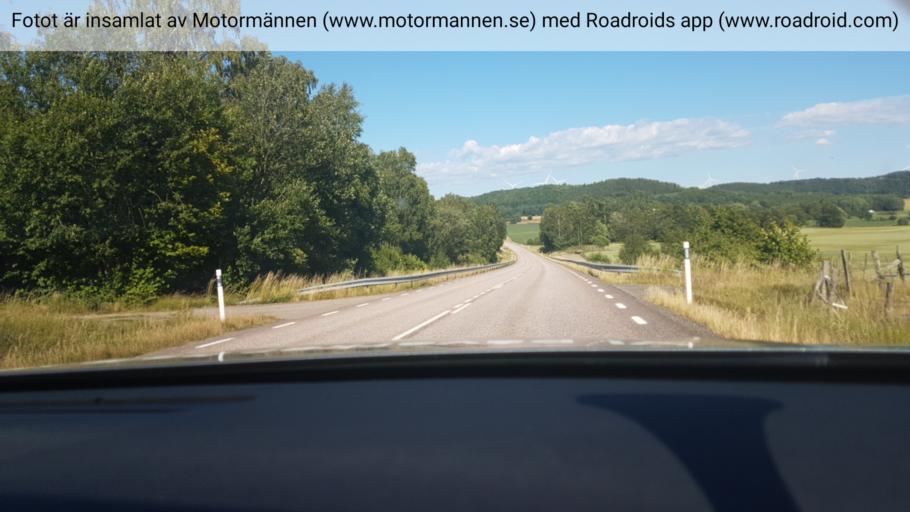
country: SE
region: Halland
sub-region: Halmstads Kommun
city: Getinge
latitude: 56.9212
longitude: 12.6921
